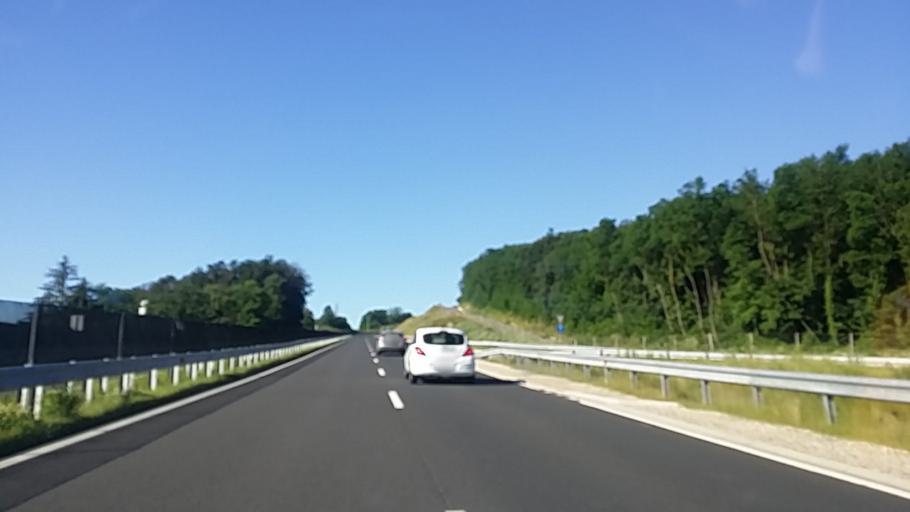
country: HU
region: Zala
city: Heviz
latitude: 46.7928
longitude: 17.1405
